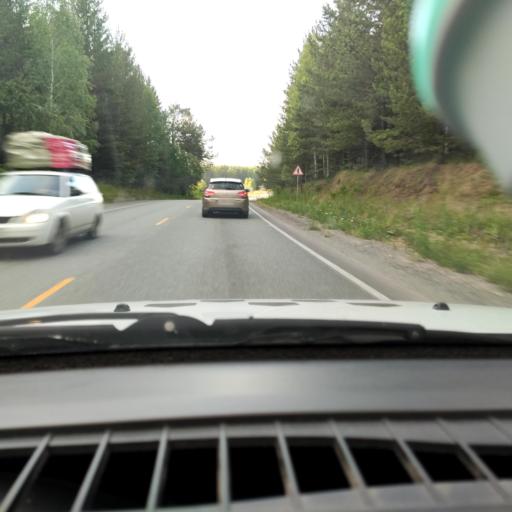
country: RU
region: Chelyabinsk
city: Turgoyak
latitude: 55.2636
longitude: 60.1973
